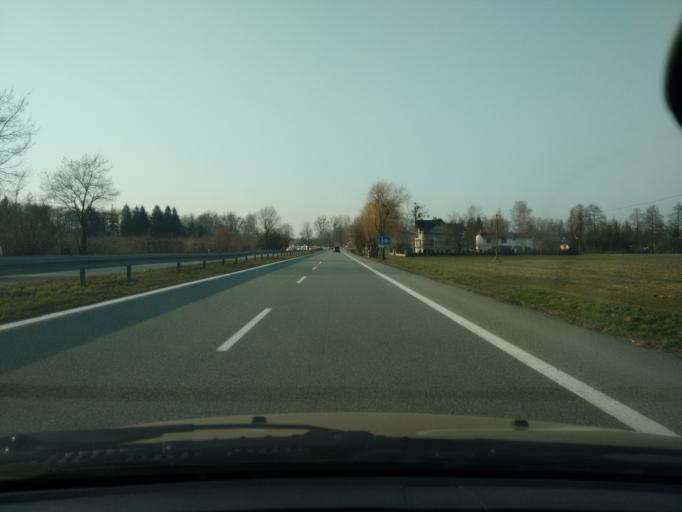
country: PL
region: Silesian Voivodeship
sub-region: Powiat cieszynski
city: Drogomysl
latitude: 49.8959
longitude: 18.7445
